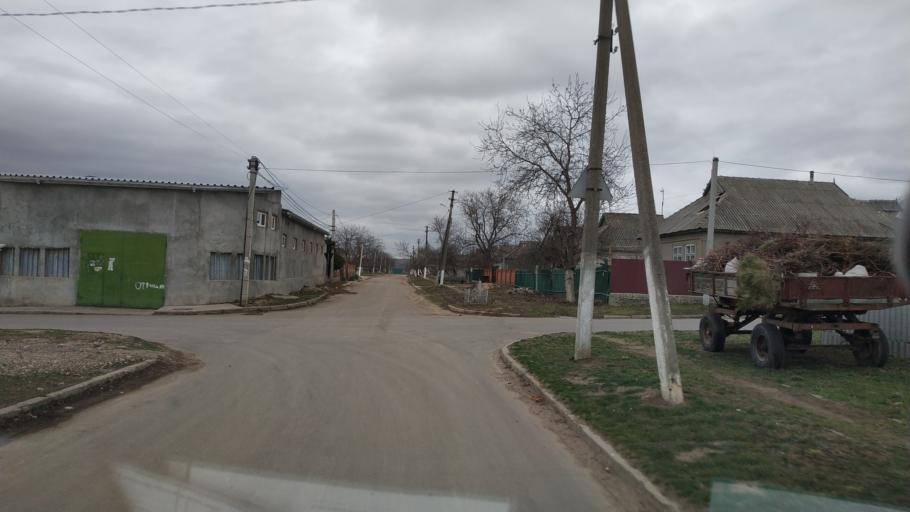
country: MD
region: Bender
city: Bender
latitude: 46.7765
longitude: 29.4803
